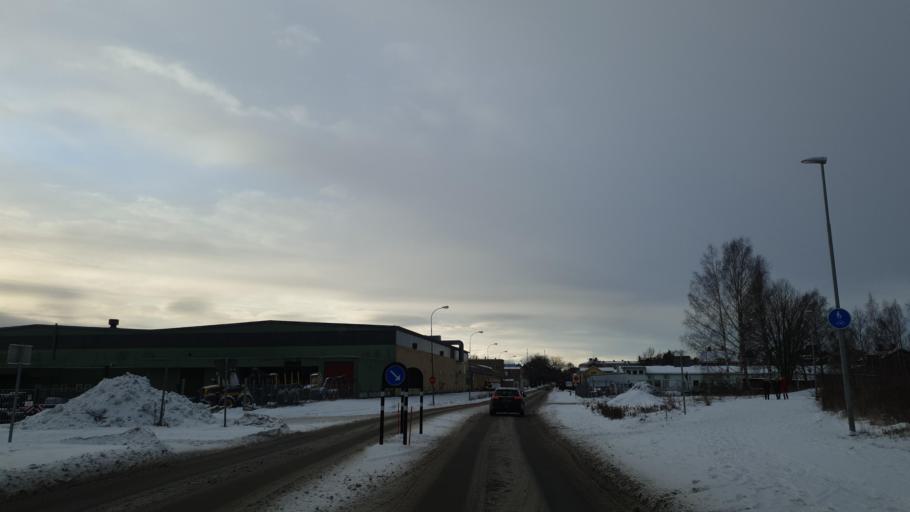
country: SE
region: Gaevleborg
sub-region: Soderhamns Kommun
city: Soderhamn
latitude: 61.3096
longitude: 17.0723
